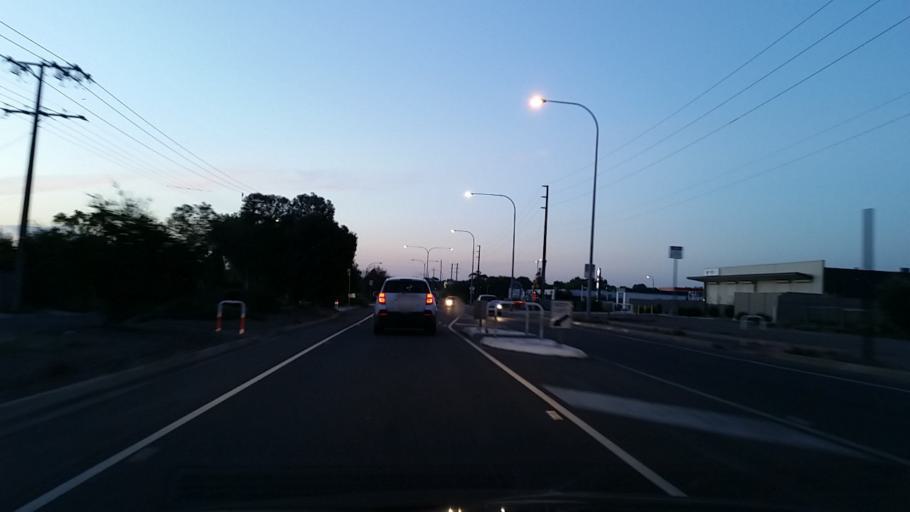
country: AU
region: South Australia
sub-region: Adelaide
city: Port Noarlunga
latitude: -35.1447
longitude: 138.4867
